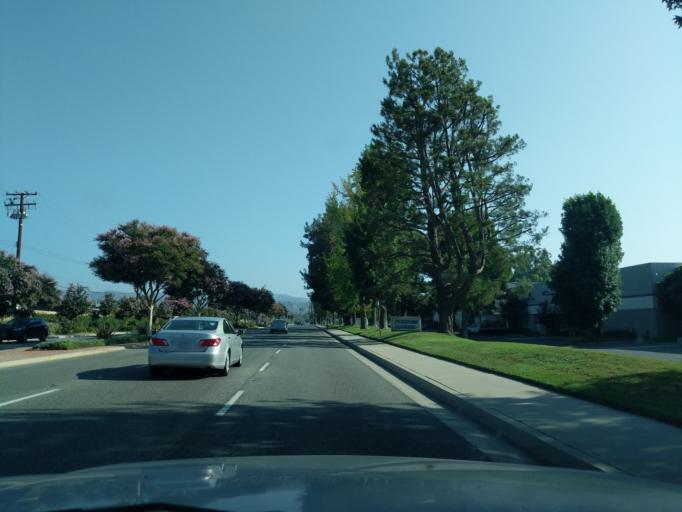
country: US
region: California
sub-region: Ventura County
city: Simi Valley
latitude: 34.2762
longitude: -118.7965
